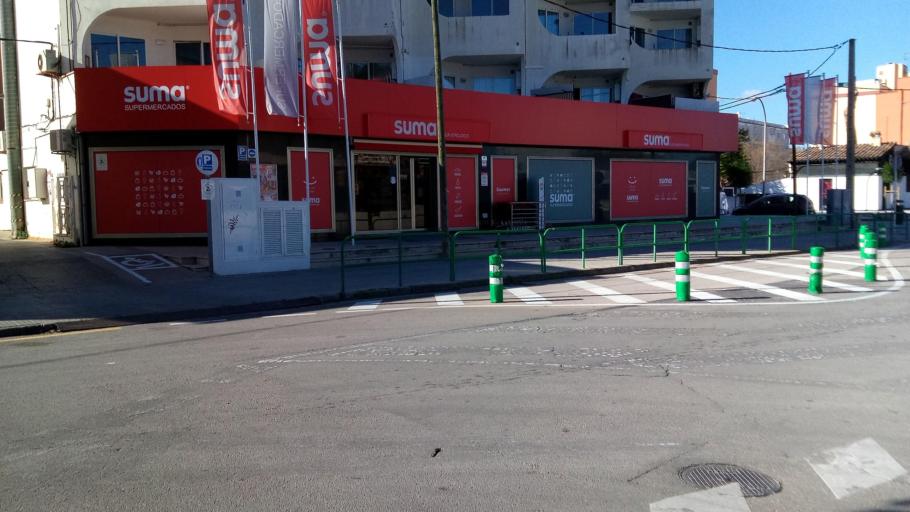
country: ES
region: Balearic Islands
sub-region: Illes Balears
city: s'Arenal
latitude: 39.5381
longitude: 2.7153
